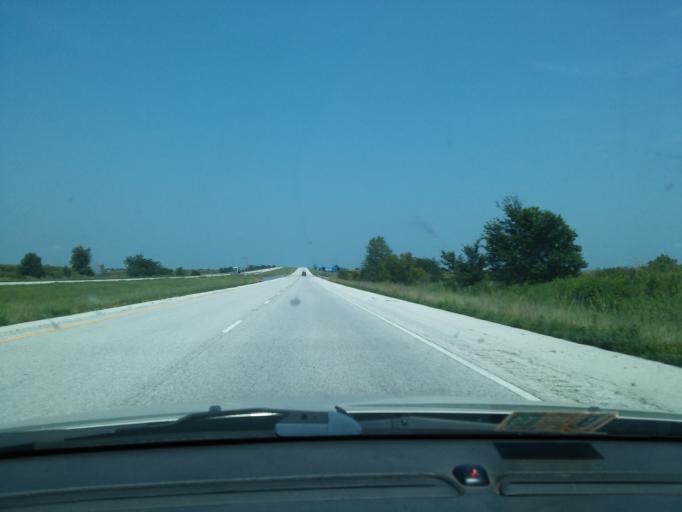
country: US
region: Illinois
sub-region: Morgan County
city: South Jacksonville
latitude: 39.7022
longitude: -90.1885
